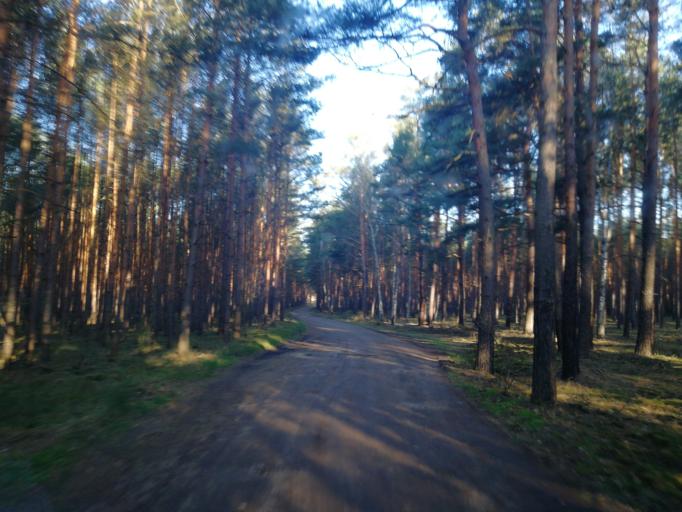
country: DE
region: Brandenburg
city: Drahnsdorf
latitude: 51.9439
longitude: 13.5701
